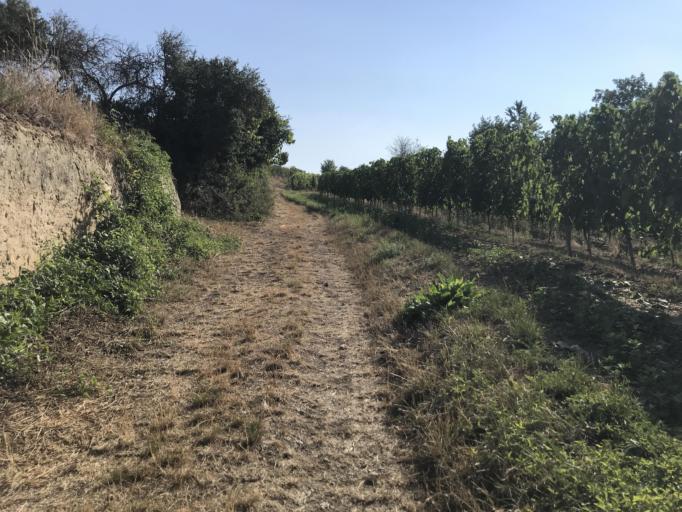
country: DE
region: Rheinland-Pfalz
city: Nieder-Ingelheim
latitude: 49.9554
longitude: 8.0755
